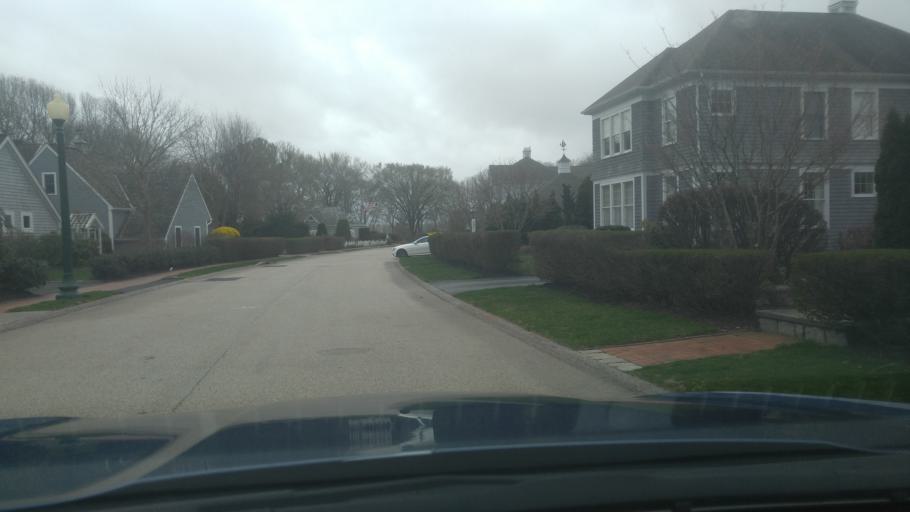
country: US
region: Rhode Island
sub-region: Washington County
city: North Kingstown
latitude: 41.5856
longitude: -71.4459
